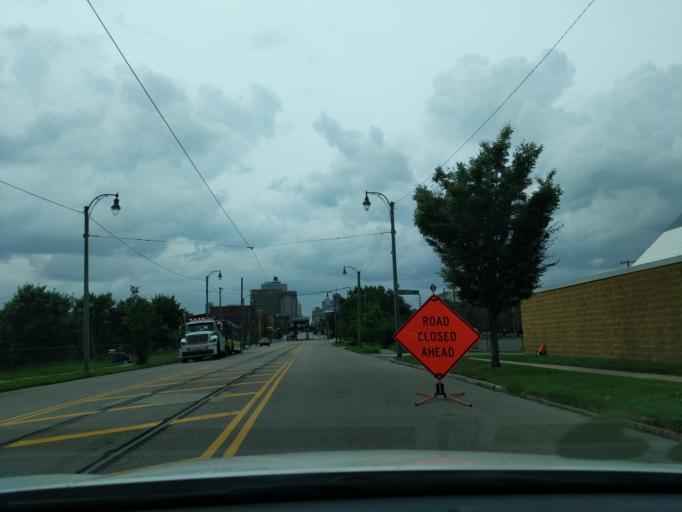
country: US
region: Tennessee
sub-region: Shelby County
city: Memphis
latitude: 35.1585
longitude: -90.0475
